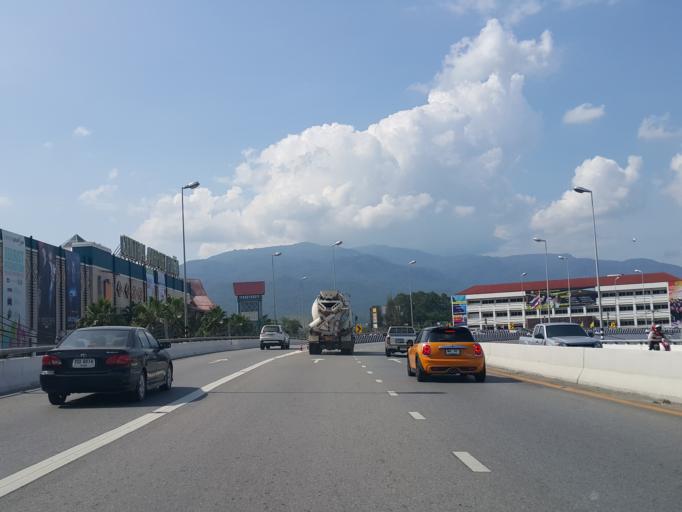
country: TH
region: Chiang Mai
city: Chiang Mai
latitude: 18.7692
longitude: 98.9767
